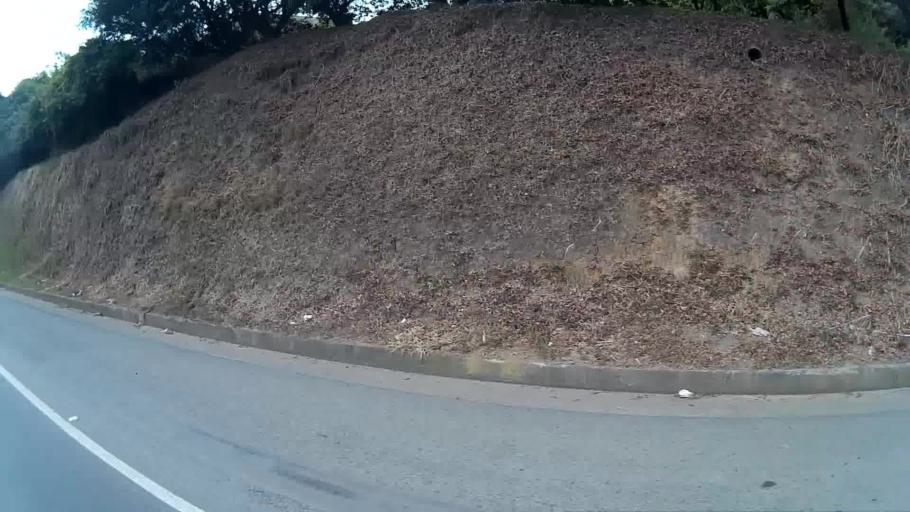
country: CO
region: Risaralda
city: Pereira
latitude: 4.8144
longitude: -75.7655
